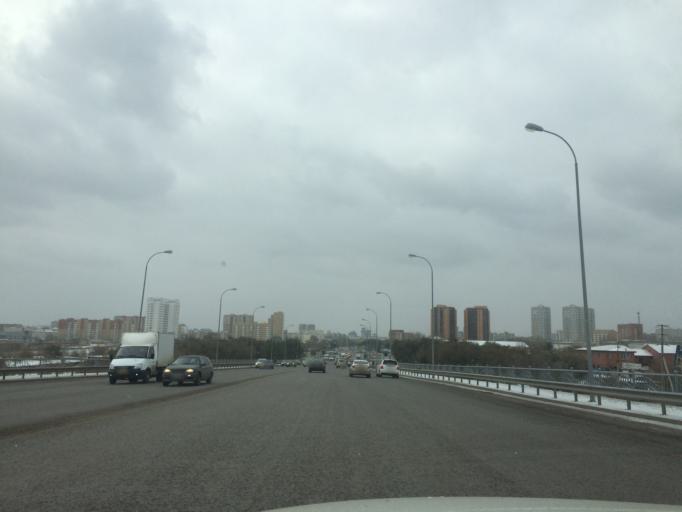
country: KZ
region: Astana Qalasy
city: Astana
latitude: 51.1708
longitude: 71.4806
